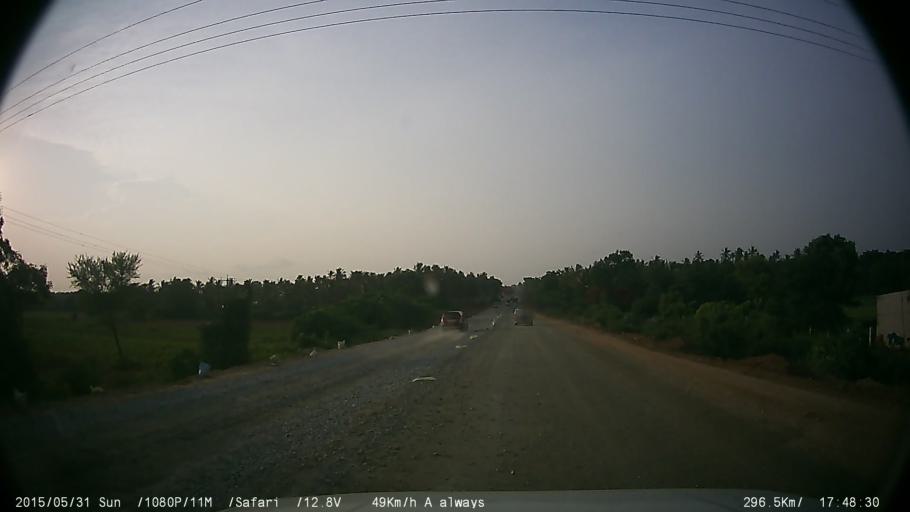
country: IN
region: Karnataka
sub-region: Mysore
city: Nanjangud
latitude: 11.9666
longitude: 76.6702
